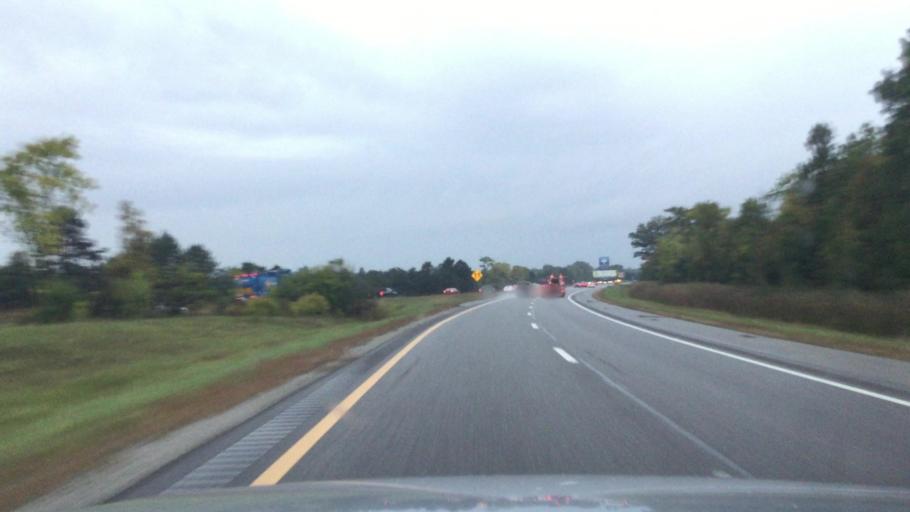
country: US
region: Michigan
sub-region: Genesee County
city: Flint
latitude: 42.9517
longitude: -83.7224
